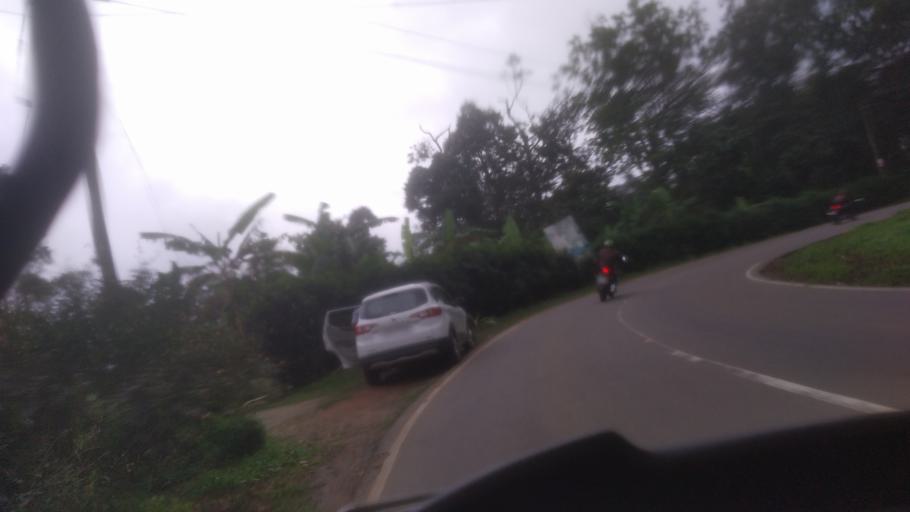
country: IN
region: Tamil Nadu
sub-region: Theni
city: Kombai
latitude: 9.8942
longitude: 77.1651
